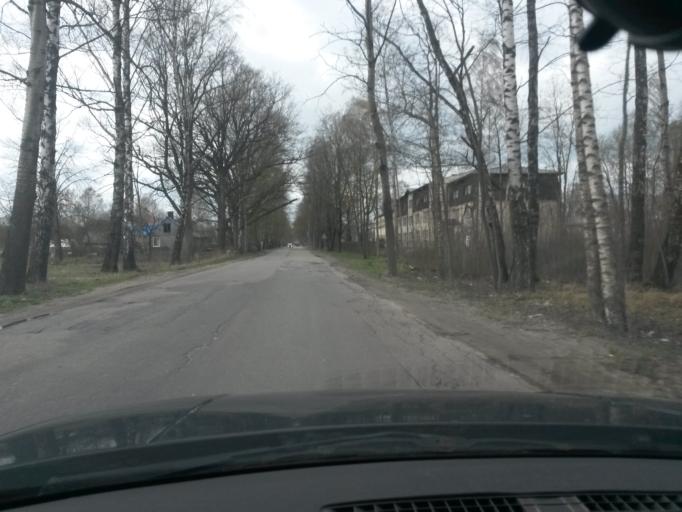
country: LV
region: Kekava
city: Kekava
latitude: 56.8934
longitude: 24.2401
